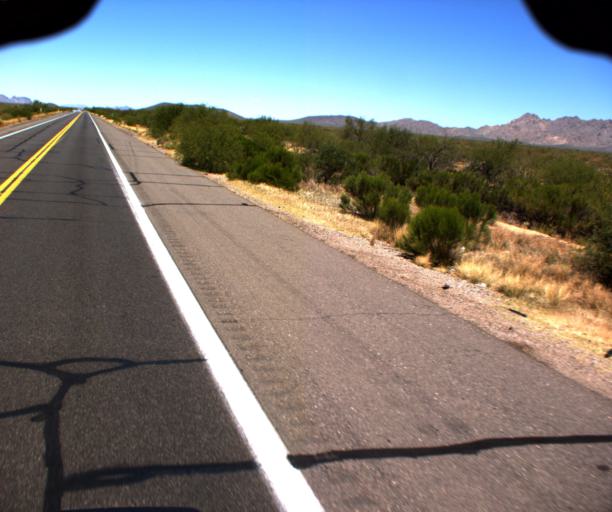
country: US
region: Arizona
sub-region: Yavapai County
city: Congress
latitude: 34.1401
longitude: -112.9745
